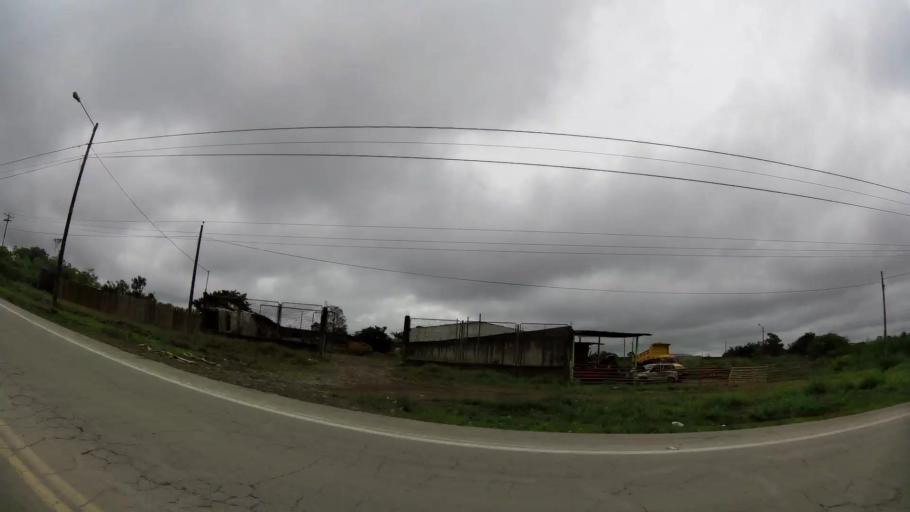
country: EC
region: Santo Domingo de los Tsachilas
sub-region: Canton Santo Domingo de los Colorados
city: Santo Domingo de los Colorados
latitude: -0.2823
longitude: -79.1888
